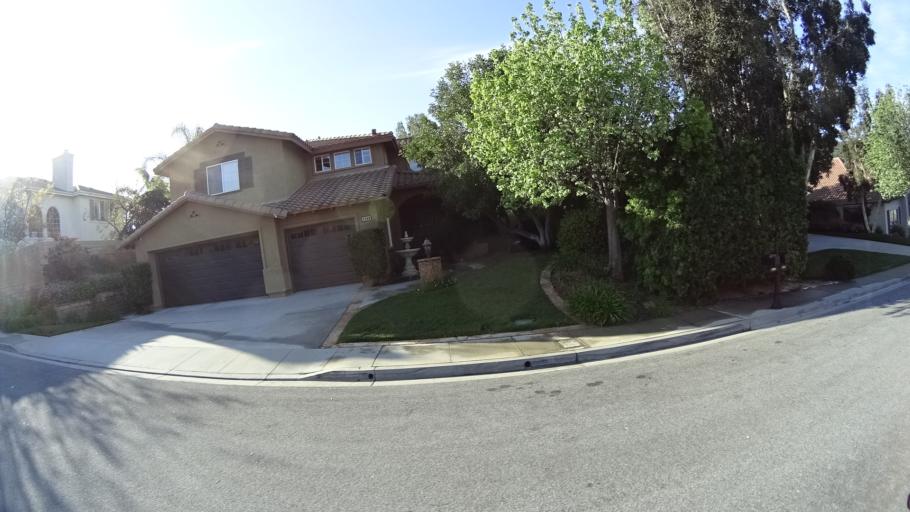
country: US
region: California
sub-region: Ventura County
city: Thousand Oaks
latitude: 34.2154
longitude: -118.8137
